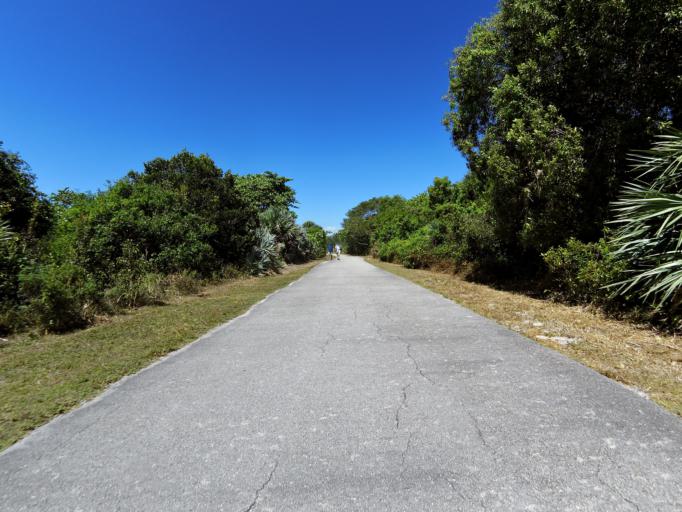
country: US
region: Florida
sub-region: Miami-Dade County
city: Key Biscayne
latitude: 25.6761
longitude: -80.1595
